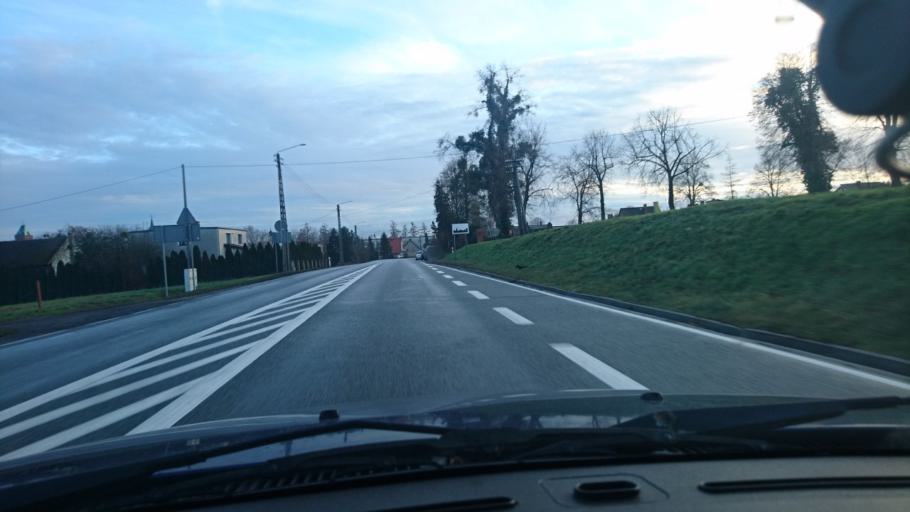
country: PL
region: Opole Voivodeship
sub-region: Powiat kluczborski
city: Byczyna
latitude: 51.1176
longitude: 18.2084
